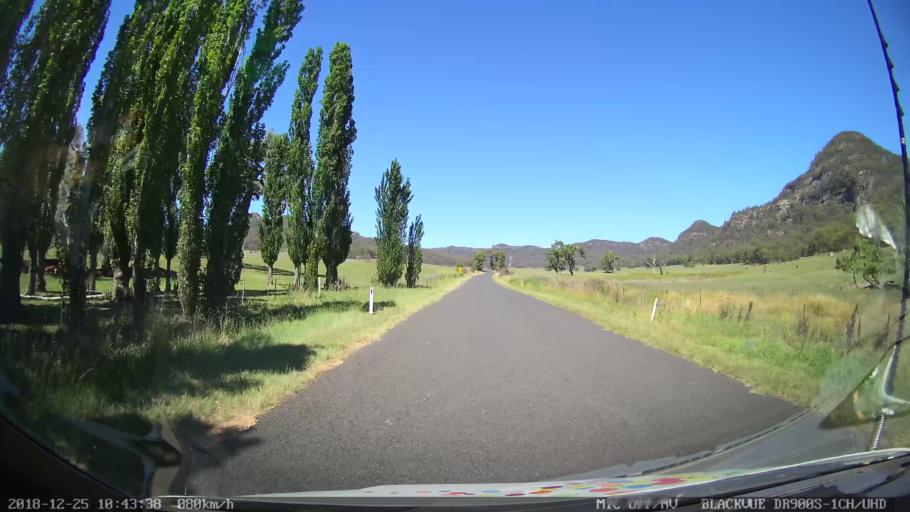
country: AU
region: New South Wales
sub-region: Upper Hunter Shire
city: Merriwa
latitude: -32.4235
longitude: 150.3103
